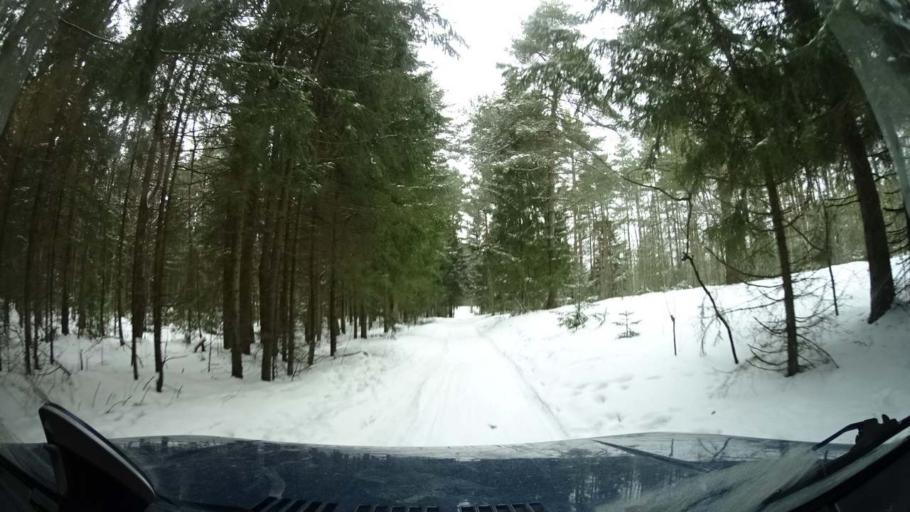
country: RU
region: Tverskaya
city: Radchenko
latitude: 56.6724
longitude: 36.4631
